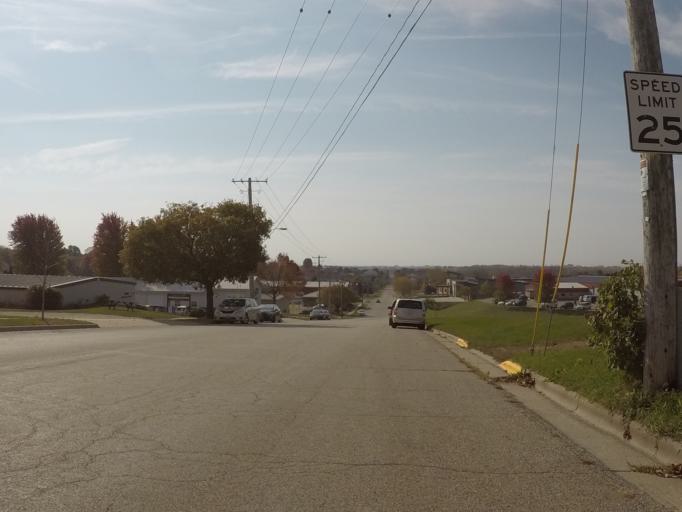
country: US
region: Wisconsin
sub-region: Dane County
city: Mount Horeb
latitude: 43.0065
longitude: -89.7453
